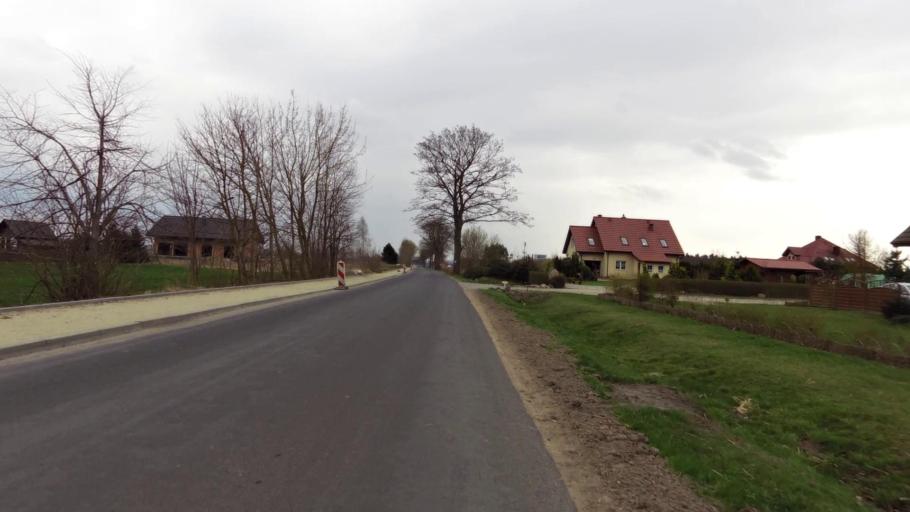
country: PL
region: West Pomeranian Voivodeship
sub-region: Powiat koszalinski
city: Sianow
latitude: 54.2817
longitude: 16.2187
